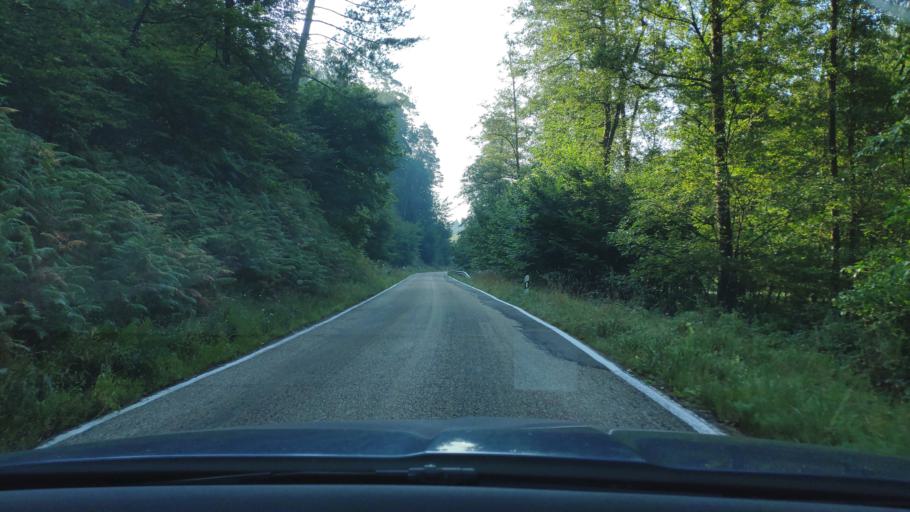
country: DE
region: Rheinland-Pfalz
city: Ludwigswinkel
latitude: 49.0979
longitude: 7.6288
